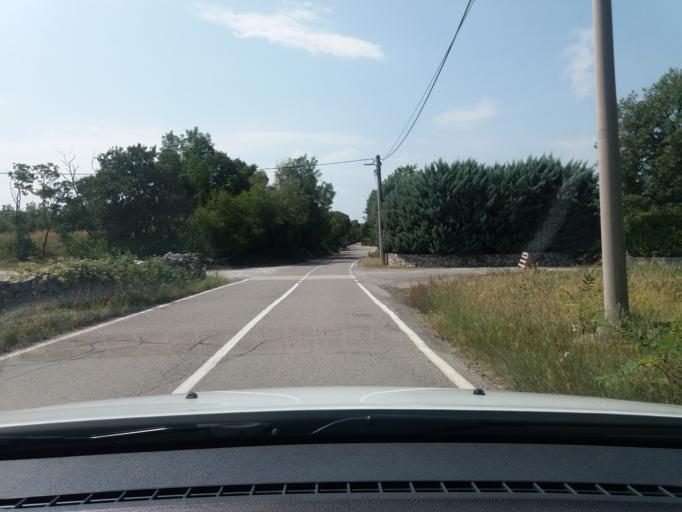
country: SI
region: Miren-Kostanjevica
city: Miren
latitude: 45.8562
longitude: 13.5849
